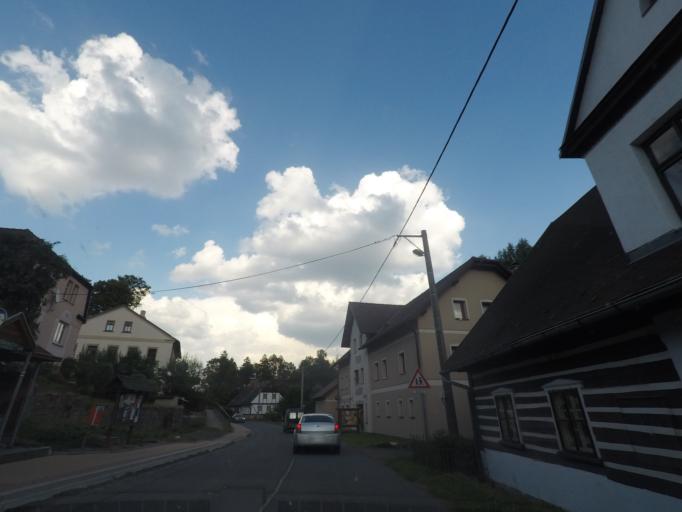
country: CZ
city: Teplice nad Metuji
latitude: 50.6187
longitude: 16.1084
